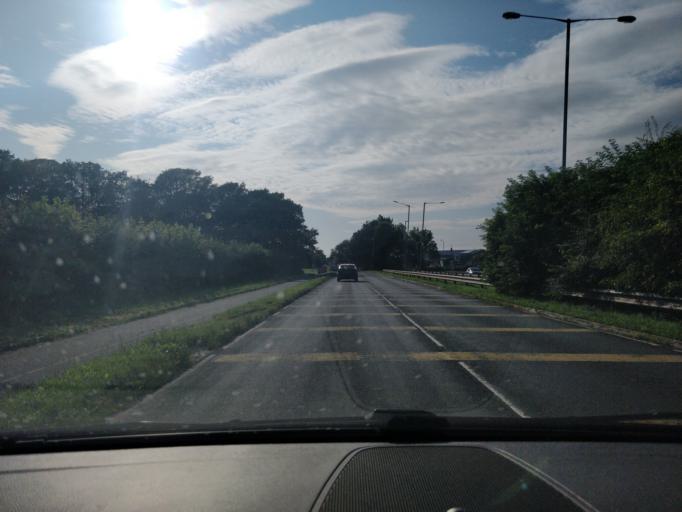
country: GB
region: England
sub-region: Lancashire
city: Banks
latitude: 53.6725
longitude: -2.9202
